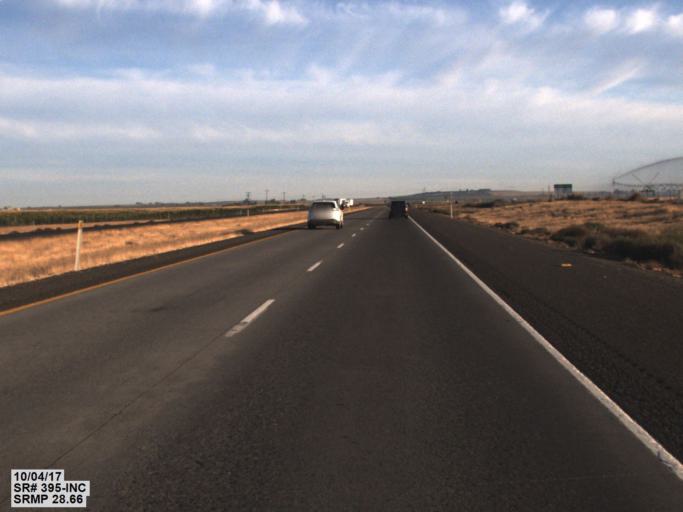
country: US
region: Washington
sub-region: Franklin County
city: Pasco
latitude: 46.3365
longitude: -119.0926
